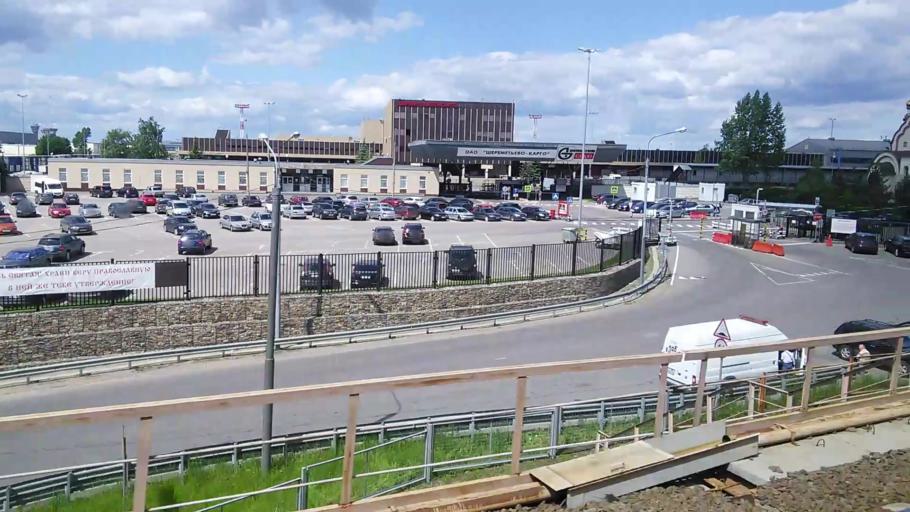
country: RU
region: Moskovskaya
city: Sheremet'yevskiy
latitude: 55.9669
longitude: 37.4365
